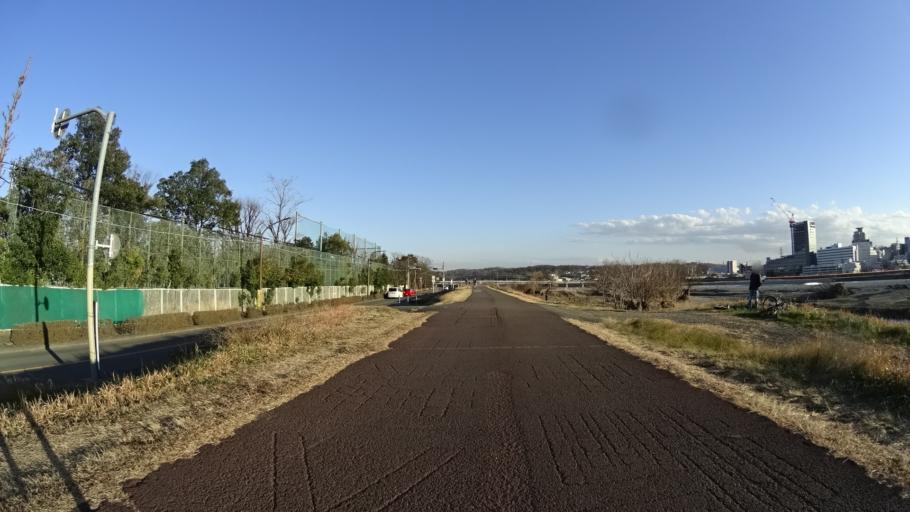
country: JP
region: Tokyo
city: Hino
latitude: 35.6581
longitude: 139.4460
